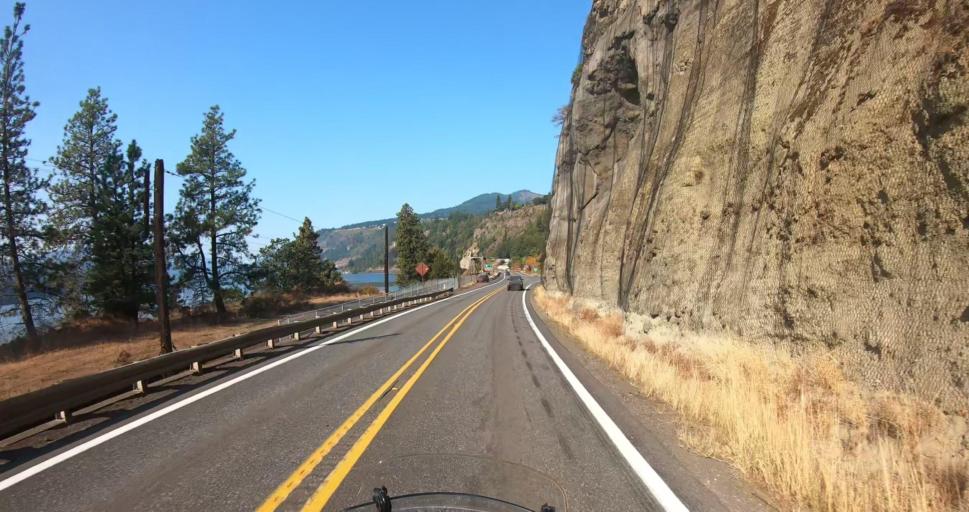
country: US
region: Oregon
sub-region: Hood River County
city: Hood River
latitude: 45.7281
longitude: -121.5195
